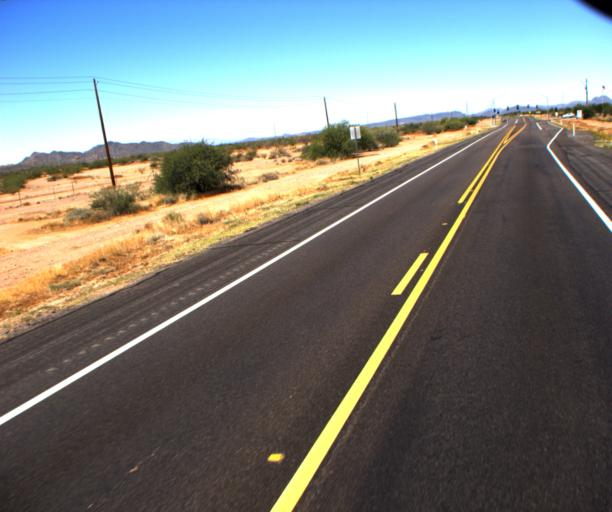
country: US
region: Arizona
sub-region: Maricopa County
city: Anthem
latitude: 33.7982
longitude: -112.1633
